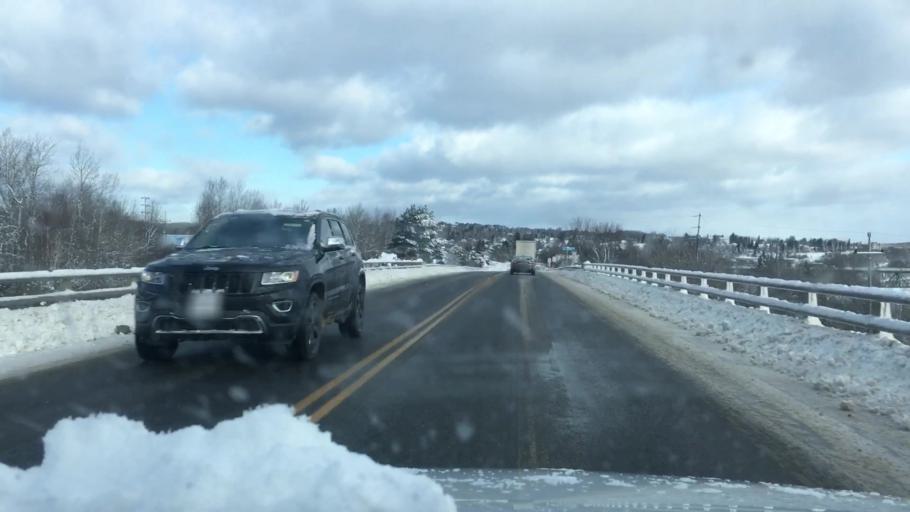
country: US
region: Maine
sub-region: Aroostook County
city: Caribou
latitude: 46.8488
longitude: -68.0047
